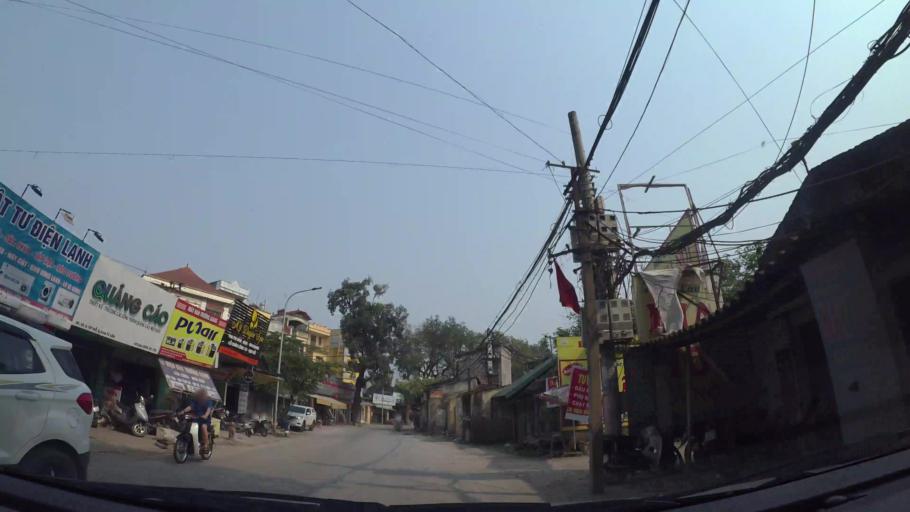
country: VN
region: Ha Noi
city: Ha Dong
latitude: 21.0000
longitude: 105.7511
